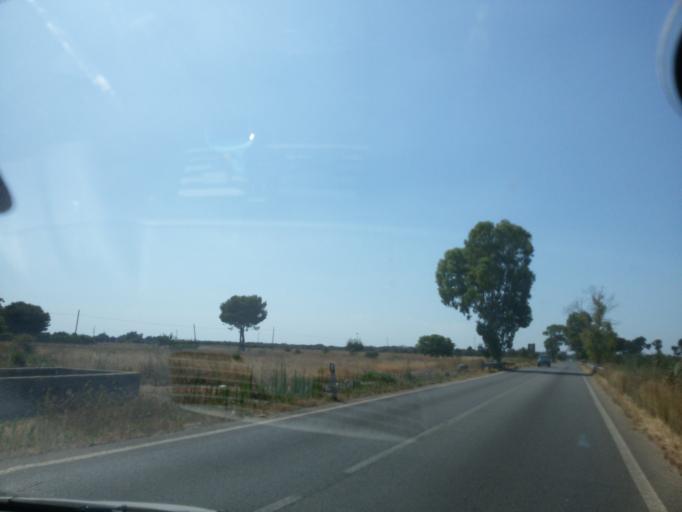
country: IT
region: Apulia
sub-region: Provincia di Lecce
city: Porto Cesareo
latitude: 40.2397
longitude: 17.9496
